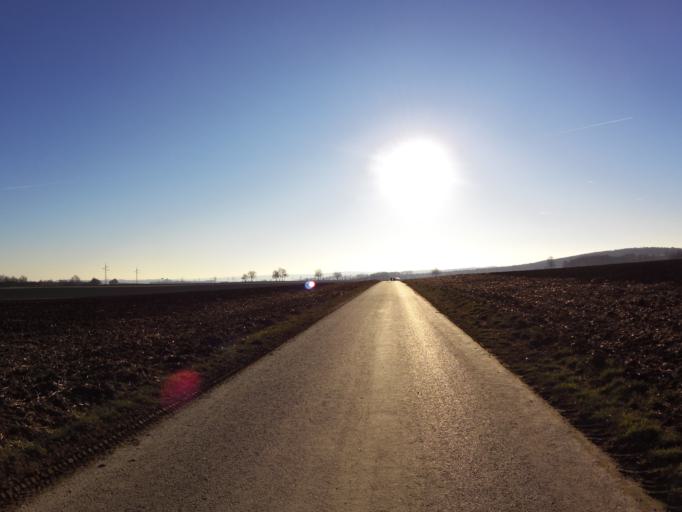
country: DE
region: Bavaria
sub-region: Regierungsbezirk Unterfranken
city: Estenfeld
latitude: 49.8402
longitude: 9.9952
